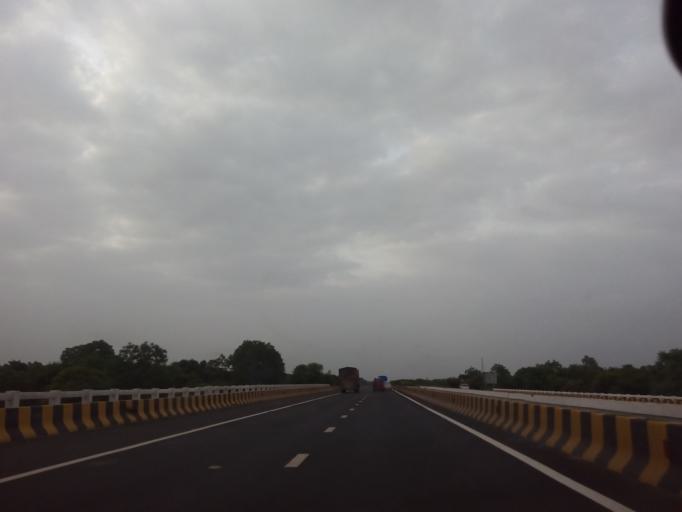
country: IN
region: Gujarat
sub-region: Kheda
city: Mahemdavad
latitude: 22.9138
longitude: 72.7622
